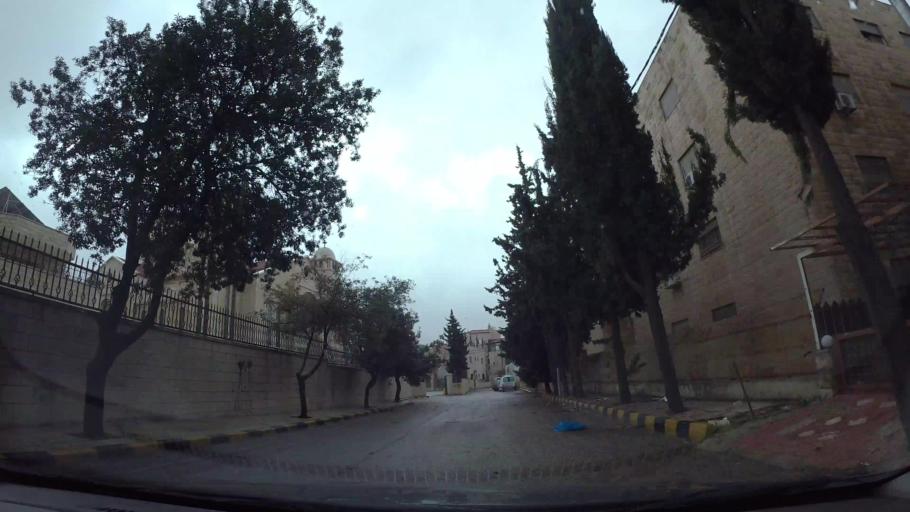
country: JO
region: Amman
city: Wadi as Sir
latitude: 31.9736
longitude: 35.8494
